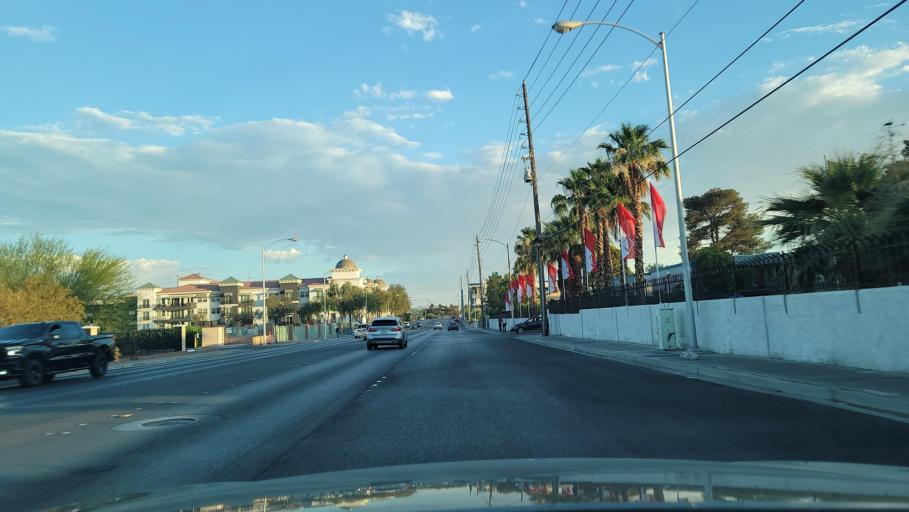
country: US
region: Nevada
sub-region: Clark County
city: Paradise
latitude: 36.1182
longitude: -115.1463
